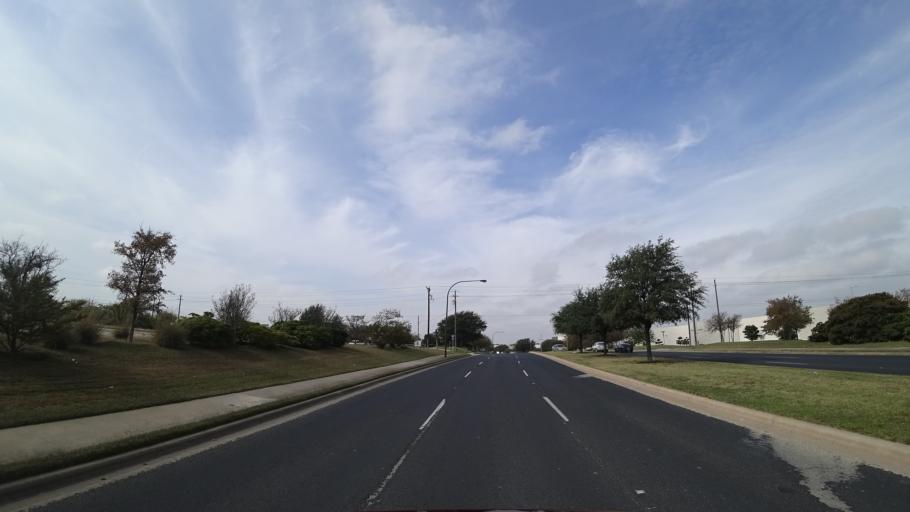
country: US
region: Texas
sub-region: Travis County
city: Wells Branch
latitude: 30.4559
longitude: -97.6689
